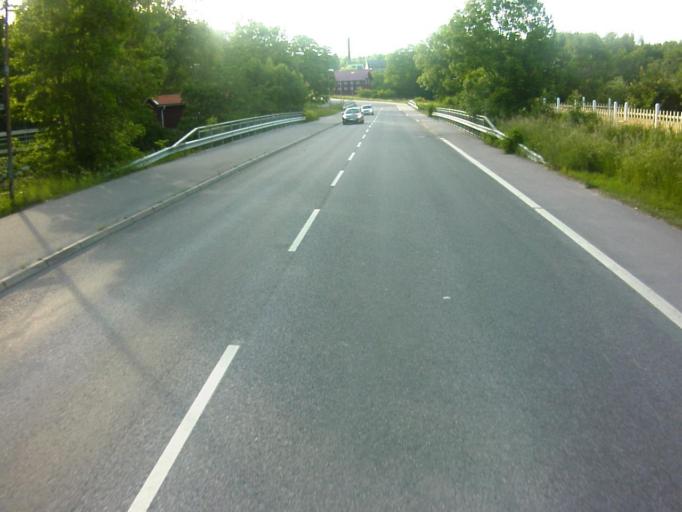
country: SE
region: Soedermanland
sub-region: Eskilstuna Kommun
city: Skogstorp
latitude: 59.3308
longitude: 16.4776
